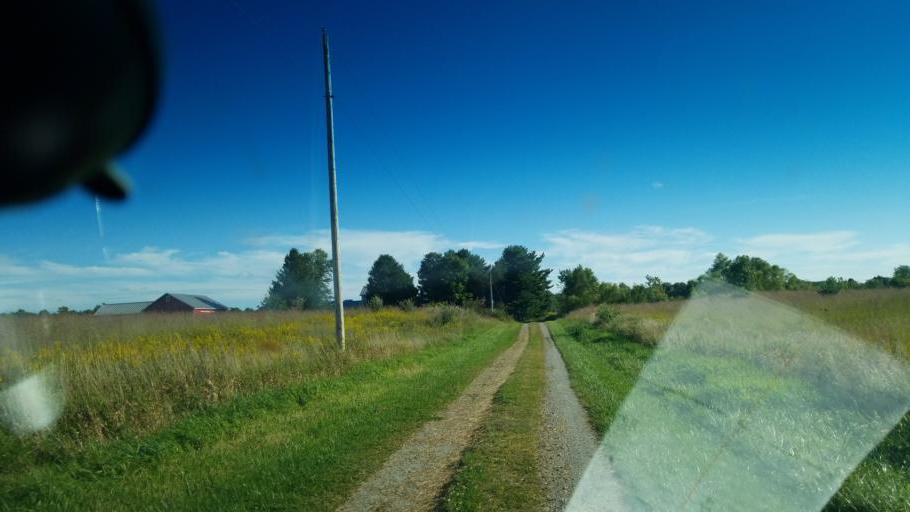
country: US
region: Ohio
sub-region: Morrow County
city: Mount Gilead
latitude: 40.6162
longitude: -82.7400
